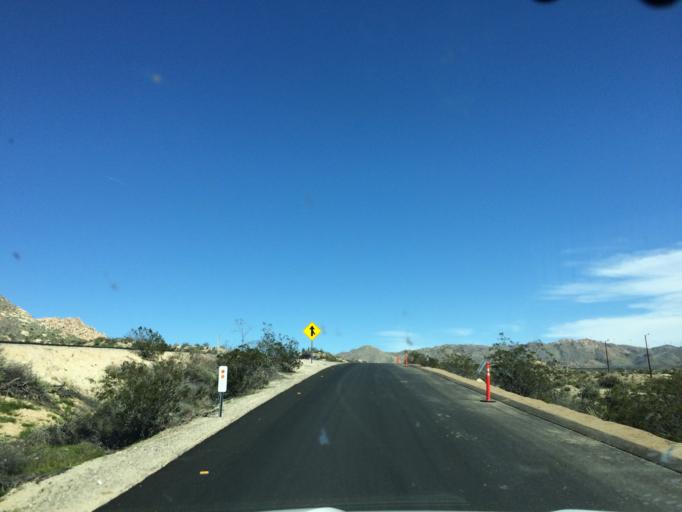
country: MX
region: Baja California
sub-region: Tecate
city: Cereso del Hongo
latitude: 32.6357
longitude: -116.1651
